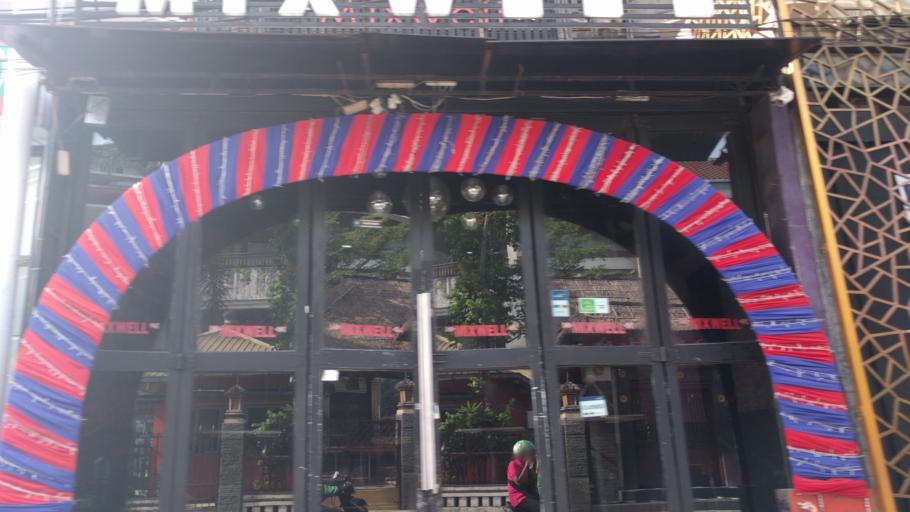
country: ID
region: Bali
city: Kuta
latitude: -8.6912
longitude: 115.1650
